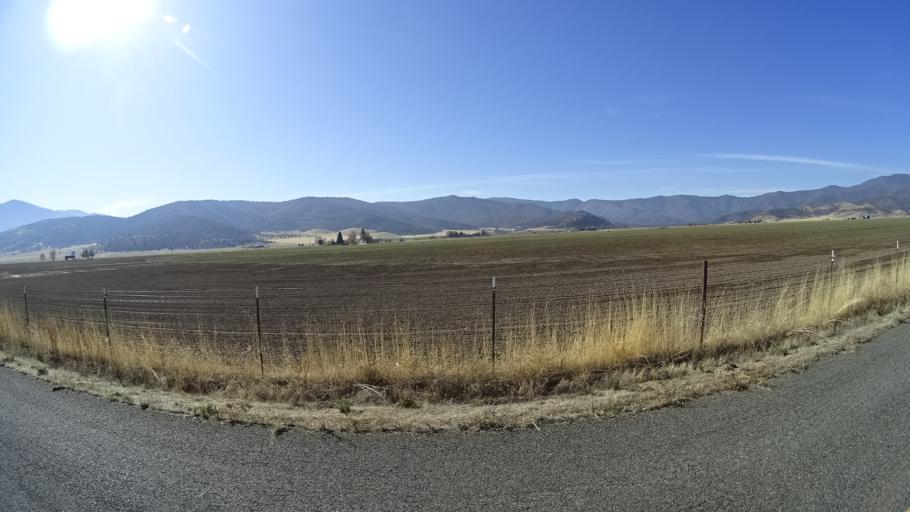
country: US
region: California
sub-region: Siskiyou County
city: Montague
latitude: 41.5409
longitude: -122.5360
